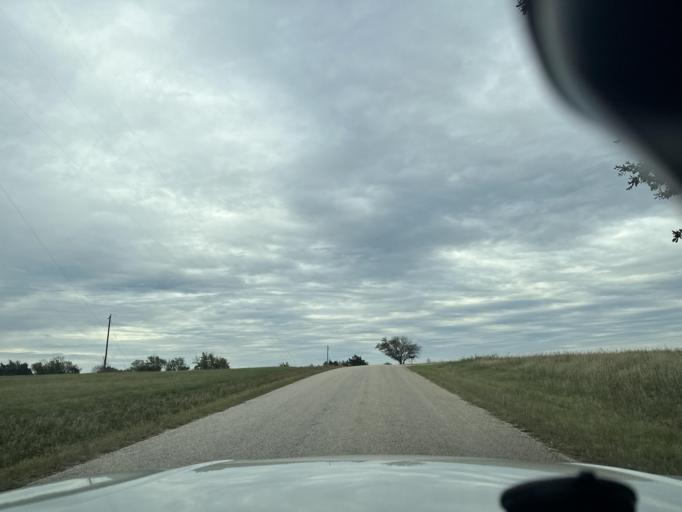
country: US
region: Texas
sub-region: Burleson County
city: Somerville
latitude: 30.1538
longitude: -96.6359
